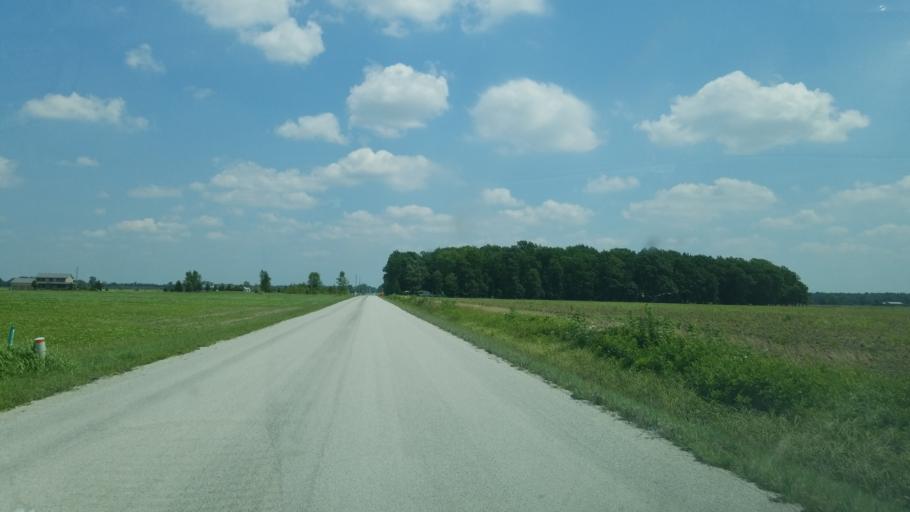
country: US
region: Ohio
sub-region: Wood County
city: North Baltimore
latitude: 41.2392
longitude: -83.5673
